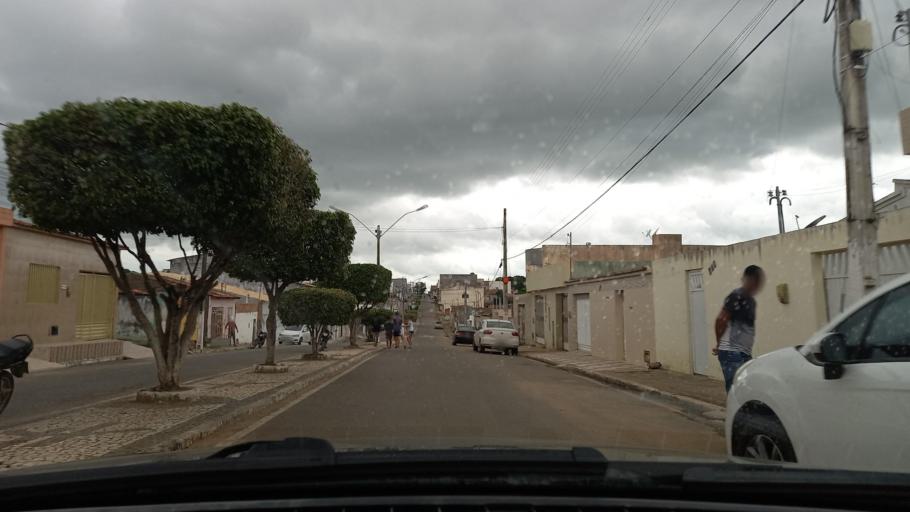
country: BR
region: Sergipe
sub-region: Caninde De Sao Francisco
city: Caninde de Sao Francisco
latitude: -9.6670
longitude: -37.7902
